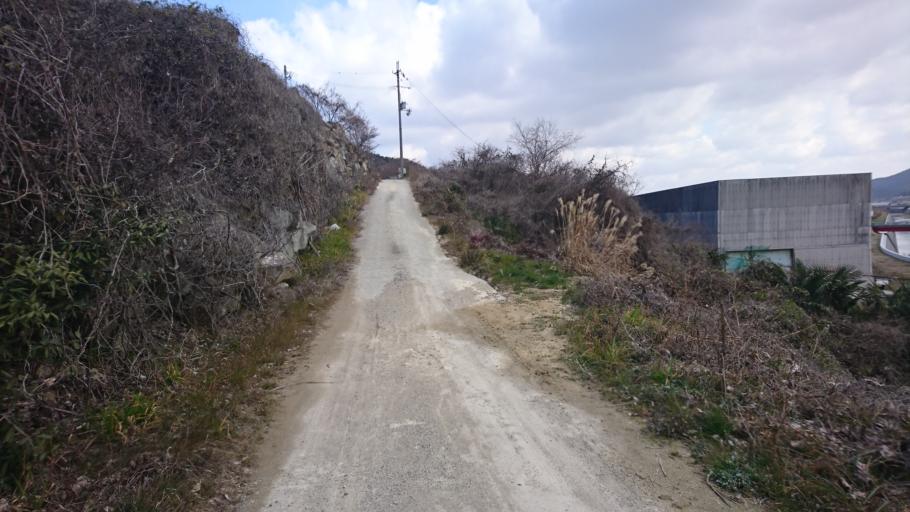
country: JP
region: Hyogo
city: Kakogawacho-honmachi
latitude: 34.7931
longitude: 134.7999
